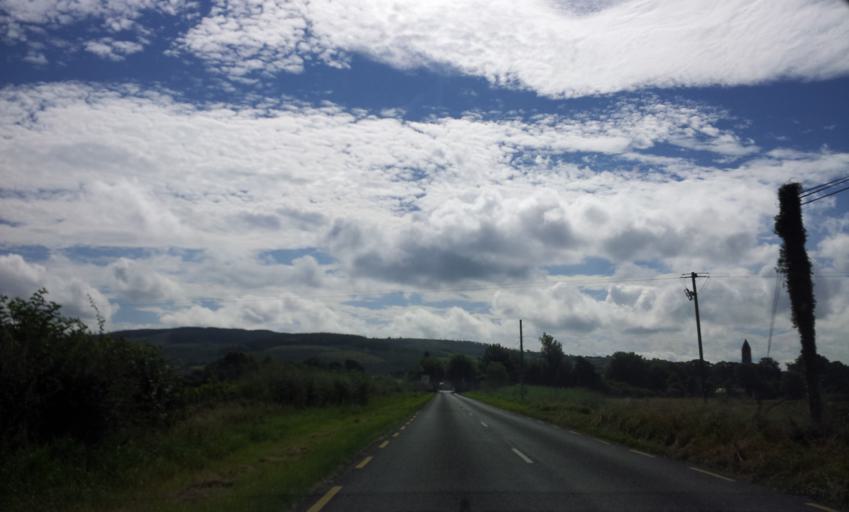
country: IE
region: Leinster
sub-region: Laois
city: Stradbally
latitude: 52.9647
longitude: -7.2046
